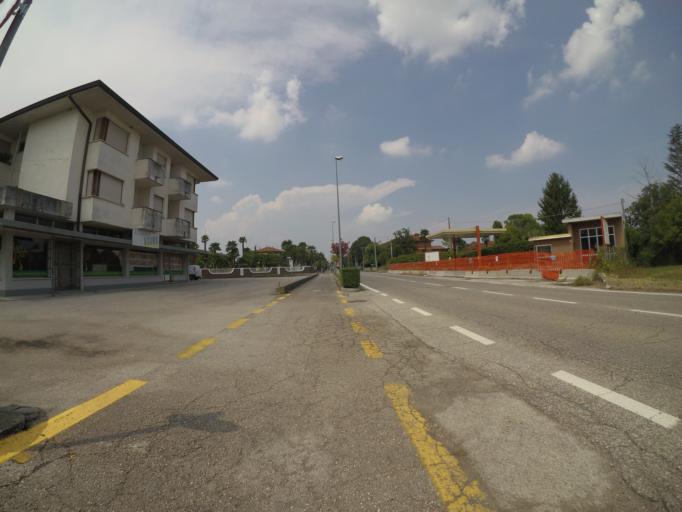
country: IT
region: Friuli Venezia Giulia
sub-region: Provincia di Udine
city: Rivignano
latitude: 45.8677
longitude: 13.0457
